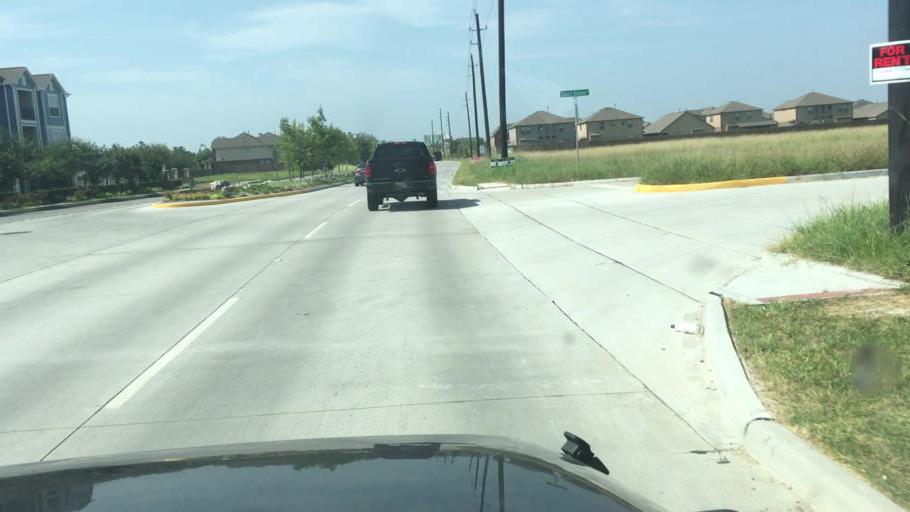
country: US
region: Texas
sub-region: Harris County
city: Atascocita
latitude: 29.9365
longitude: -95.2114
